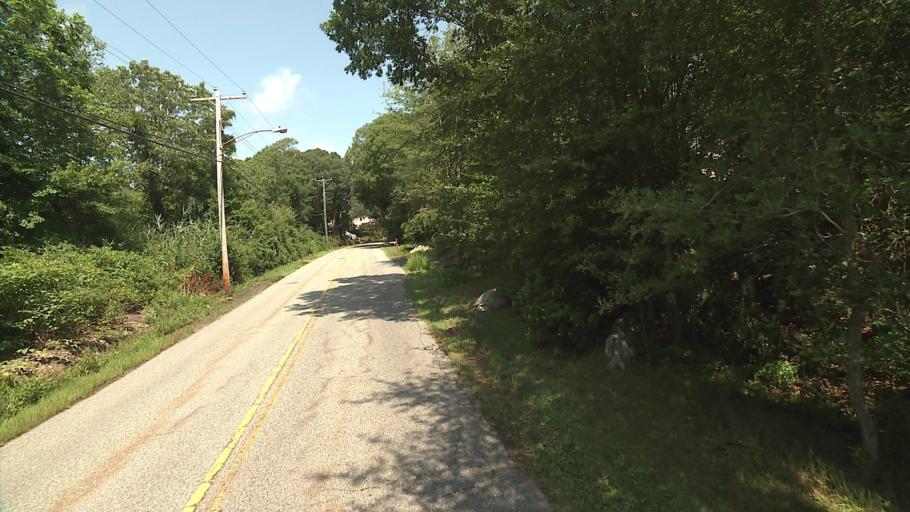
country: US
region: Connecticut
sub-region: New London County
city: Central Waterford
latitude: 41.3190
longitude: -72.1061
